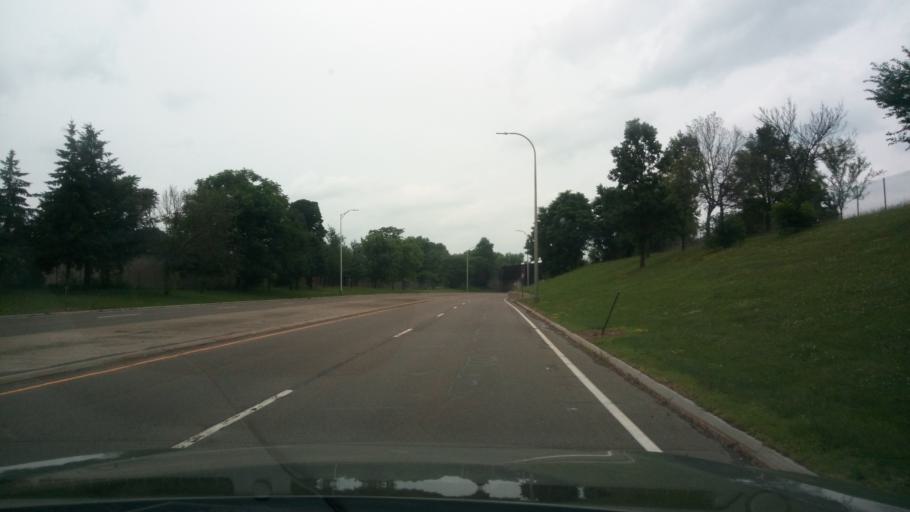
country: US
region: New York
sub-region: Chemung County
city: Elmira
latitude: 42.0774
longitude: -76.7999
